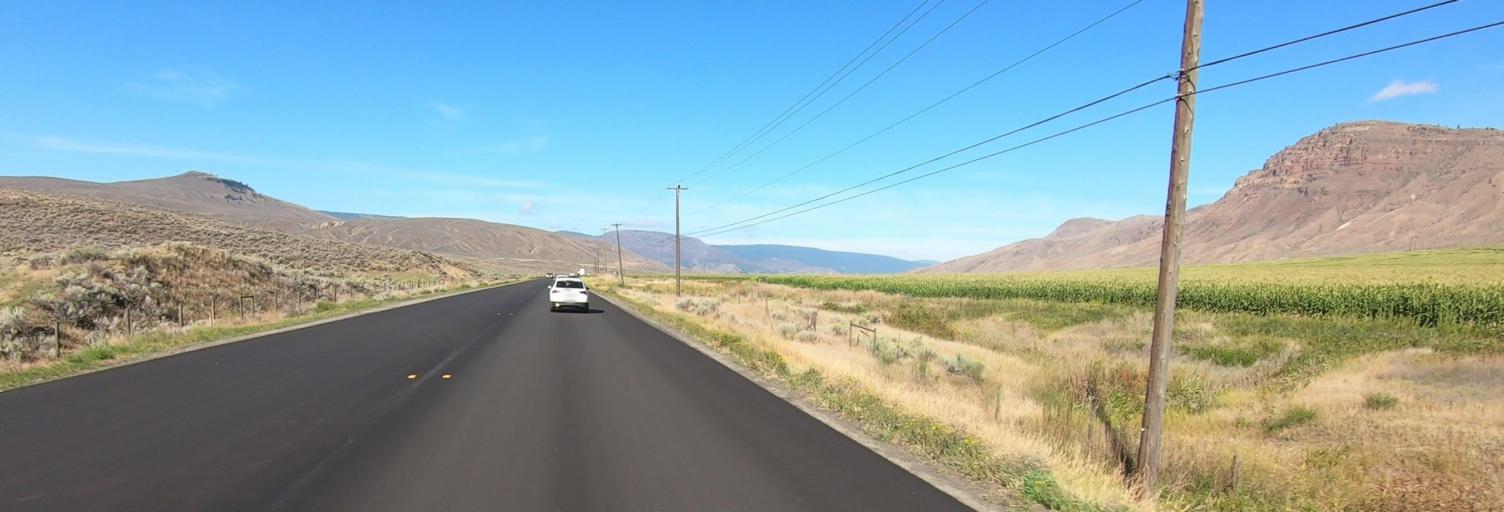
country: CA
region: British Columbia
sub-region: Thompson-Nicola Regional District
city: Ashcroft
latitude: 50.7858
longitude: -121.2034
